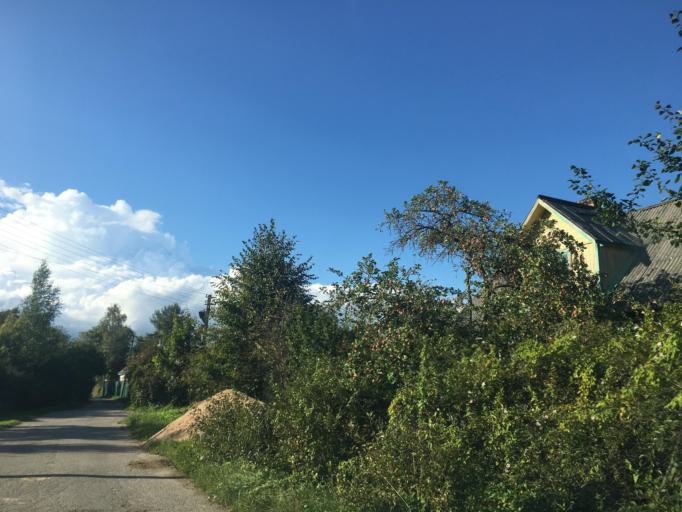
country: RU
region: Pskov
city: Izborsk
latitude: 57.7711
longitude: 27.9728
